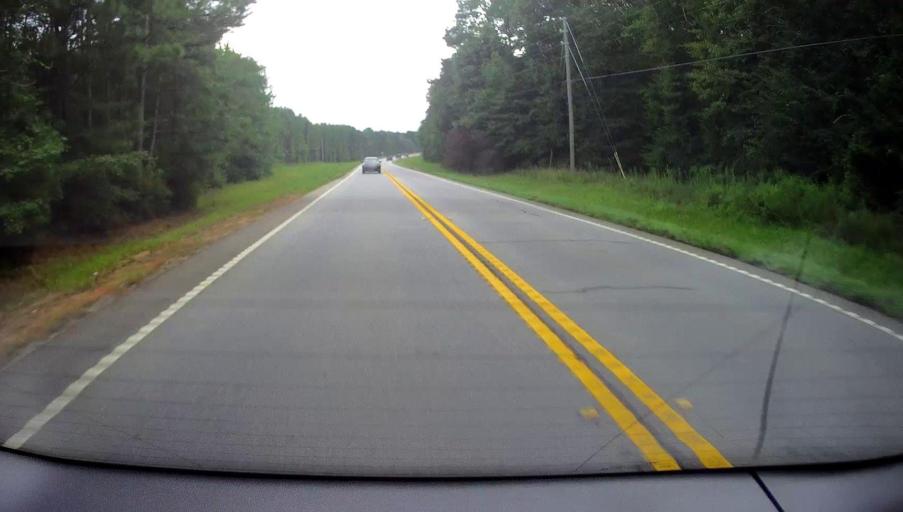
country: US
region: Georgia
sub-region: Coweta County
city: Senoia
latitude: 33.1837
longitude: -84.5806
